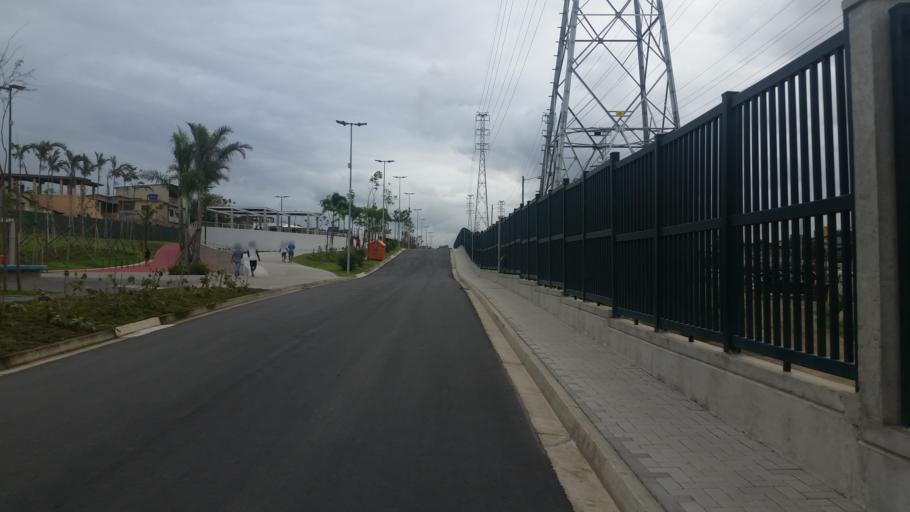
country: BR
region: Rio de Janeiro
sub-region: Sao Joao De Meriti
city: Sao Joao de Meriti
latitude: -22.8520
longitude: -43.3554
